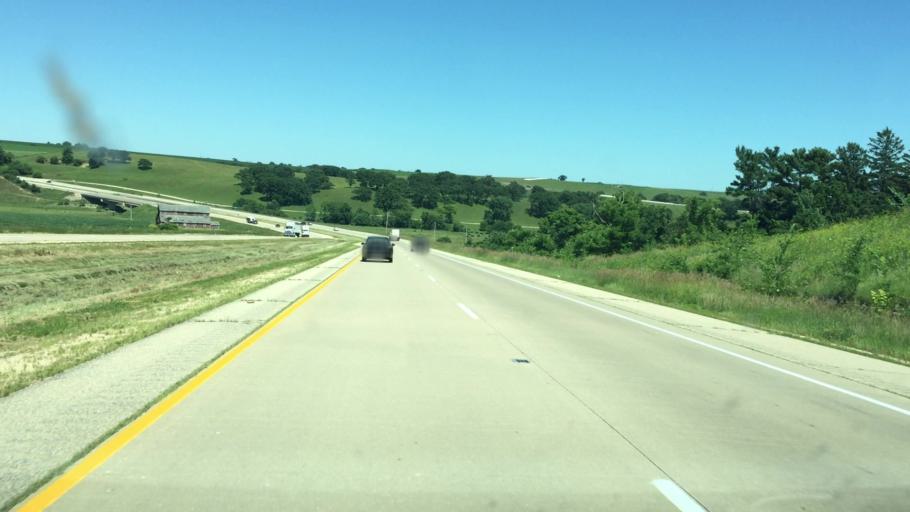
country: US
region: Wisconsin
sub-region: Iowa County
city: Mineral Point
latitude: 42.8085
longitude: -90.2653
